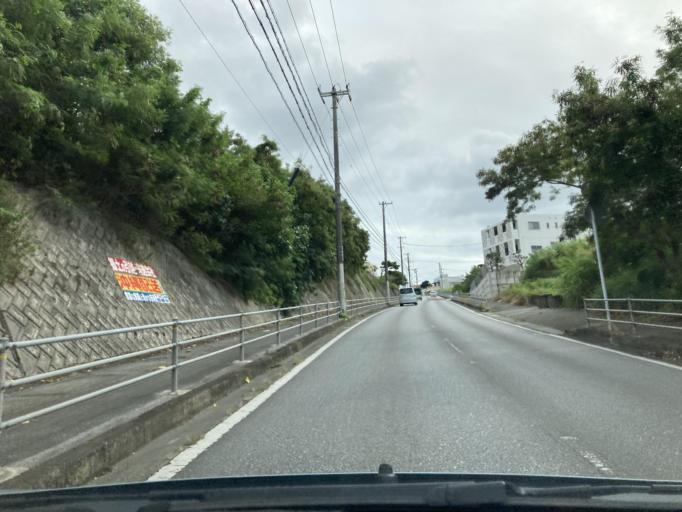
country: JP
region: Okinawa
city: Tomigusuku
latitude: 26.1635
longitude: 127.6794
